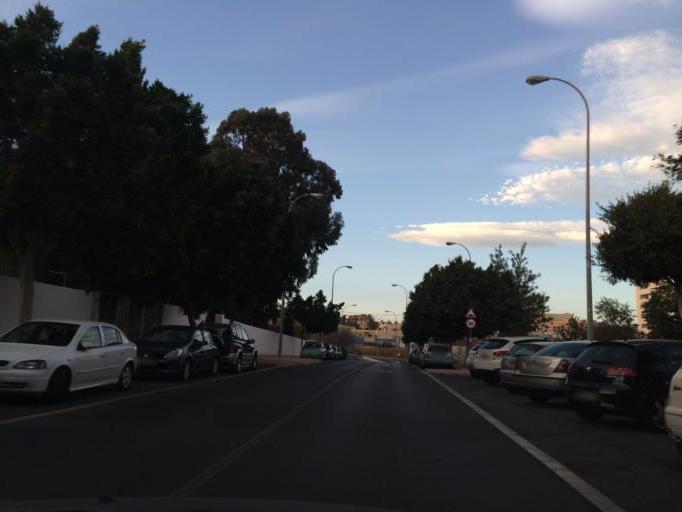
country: ES
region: Andalusia
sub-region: Provincia de Almeria
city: Almeria
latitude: 36.8543
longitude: -2.4399
